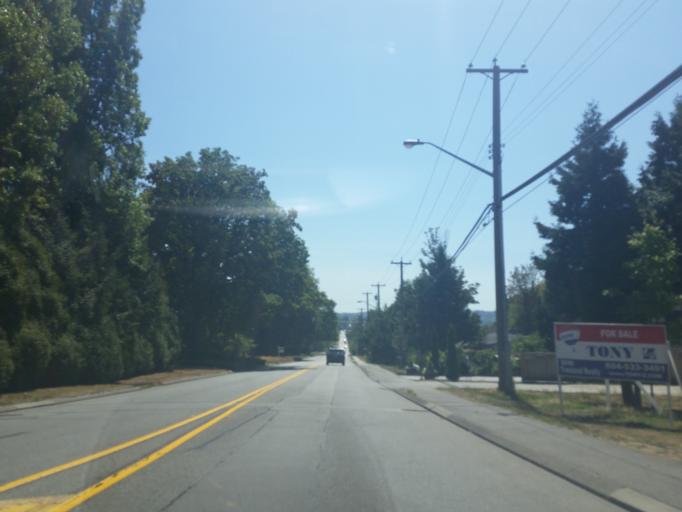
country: CA
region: British Columbia
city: Langley
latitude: 49.1025
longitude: -122.7128
